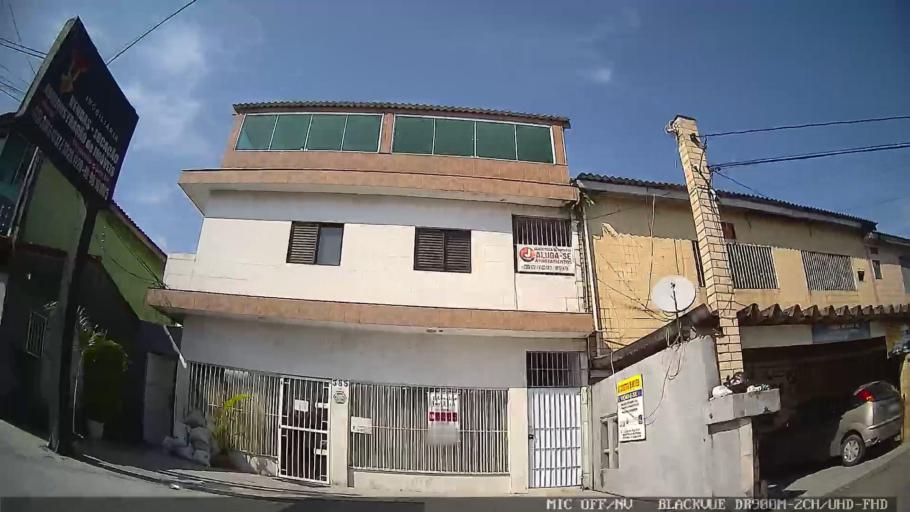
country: BR
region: Sao Paulo
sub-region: Guaruja
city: Guaruja
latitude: -23.9951
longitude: -46.2747
